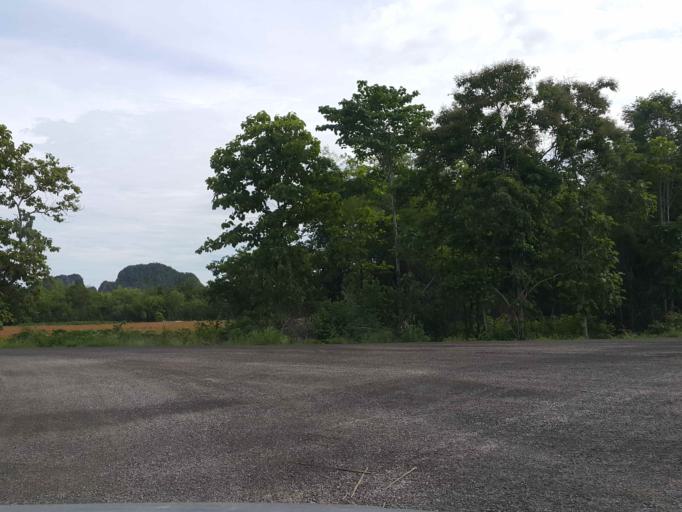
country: TH
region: Sukhothai
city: Thung Saliam
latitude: 17.2579
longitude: 99.5250
